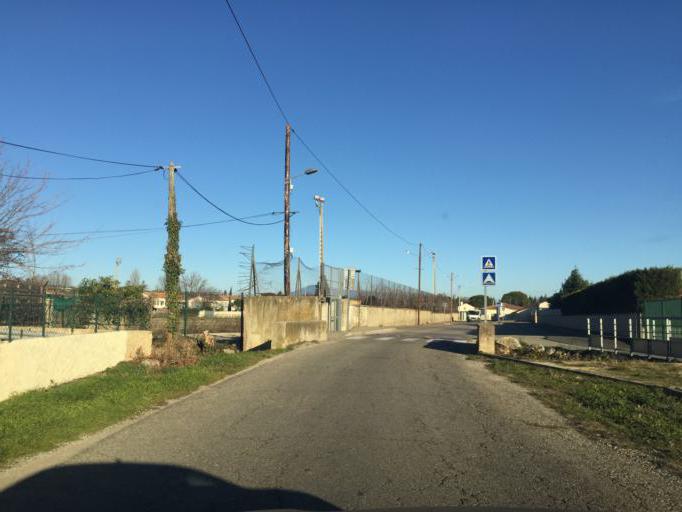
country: FR
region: Provence-Alpes-Cote d'Azur
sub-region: Departement du Vaucluse
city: Sorgues
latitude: 44.0009
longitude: 4.8831
